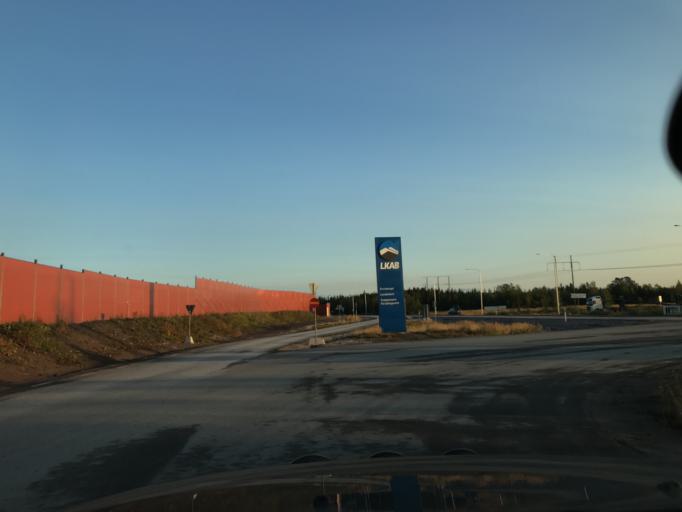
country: SE
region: Norrbotten
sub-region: Gallivare Kommun
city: Malmberget
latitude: 67.6520
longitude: 21.0160
